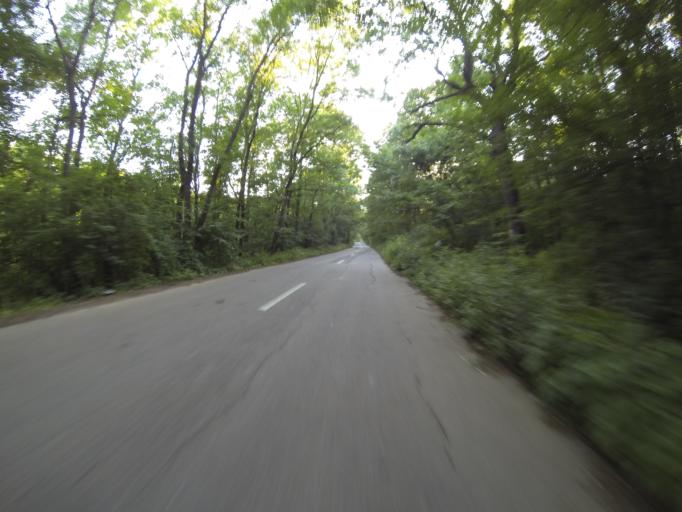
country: RO
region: Dolj
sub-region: Comuna Tuglui
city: Tuglui
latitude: 44.1620
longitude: 23.8198
